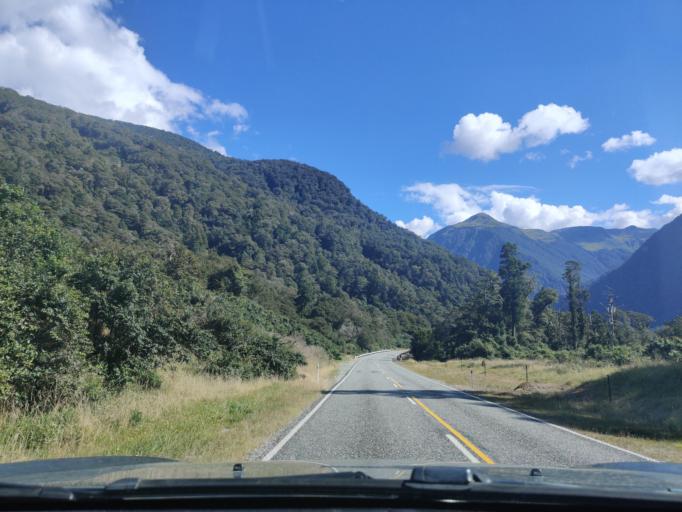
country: NZ
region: Otago
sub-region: Queenstown-Lakes District
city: Wanaka
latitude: -43.9671
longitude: 169.3759
